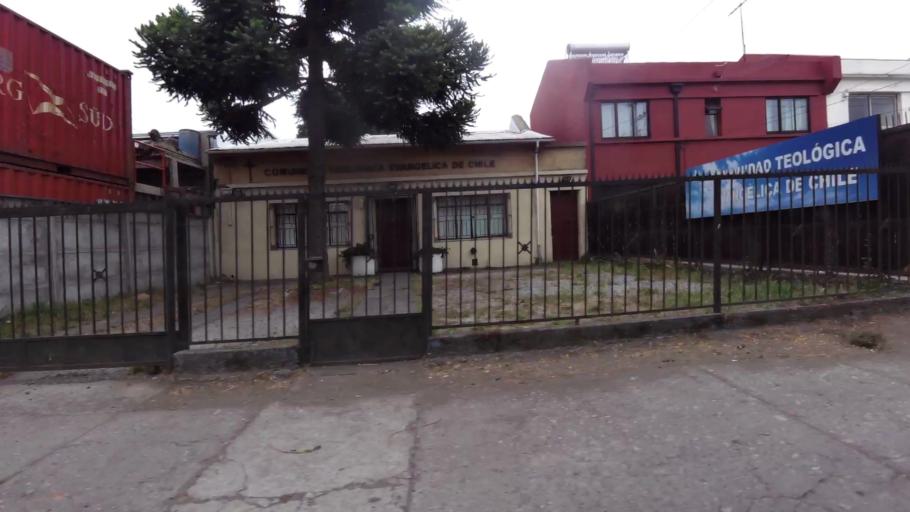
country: CL
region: Biobio
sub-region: Provincia de Concepcion
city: Concepcion
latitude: -36.8195
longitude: -73.0521
